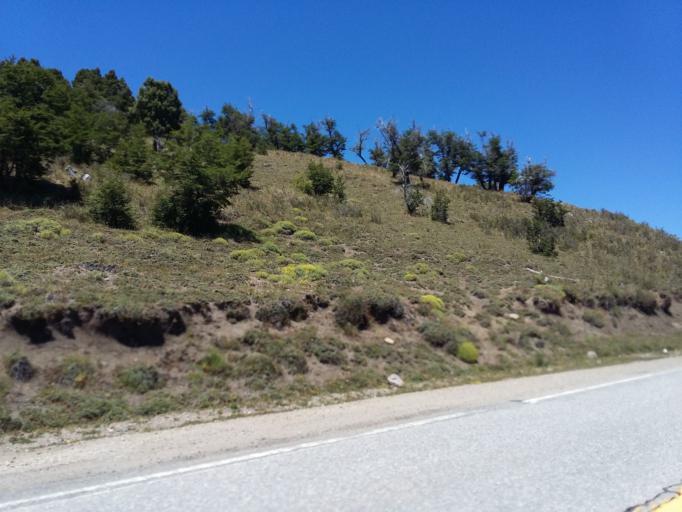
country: AR
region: Neuquen
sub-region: Departamento de Lacar
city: San Martin de los Andes
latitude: -40.1974
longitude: -71.3597
